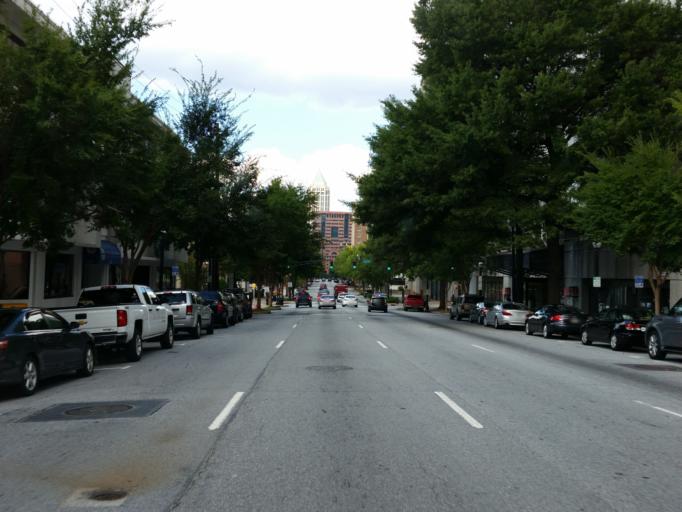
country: US
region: Georgia
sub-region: Fulton County
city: Atlanta
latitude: 33.7731
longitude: -84.3875
